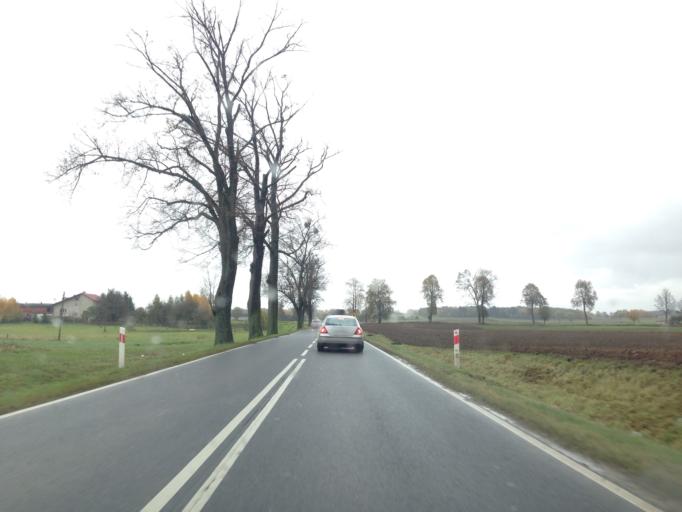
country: PL
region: Warmian-Masurian Voivodeship
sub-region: Powiat nowomiejski
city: Biskupiec
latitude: 53.6020
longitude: 19.4067
